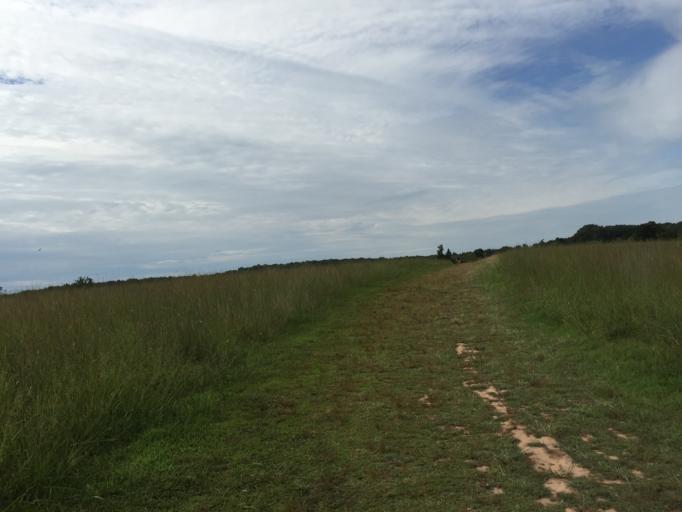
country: US
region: Virginia
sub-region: Prince William County
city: Bull Run
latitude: 38.8211
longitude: -77.5263
